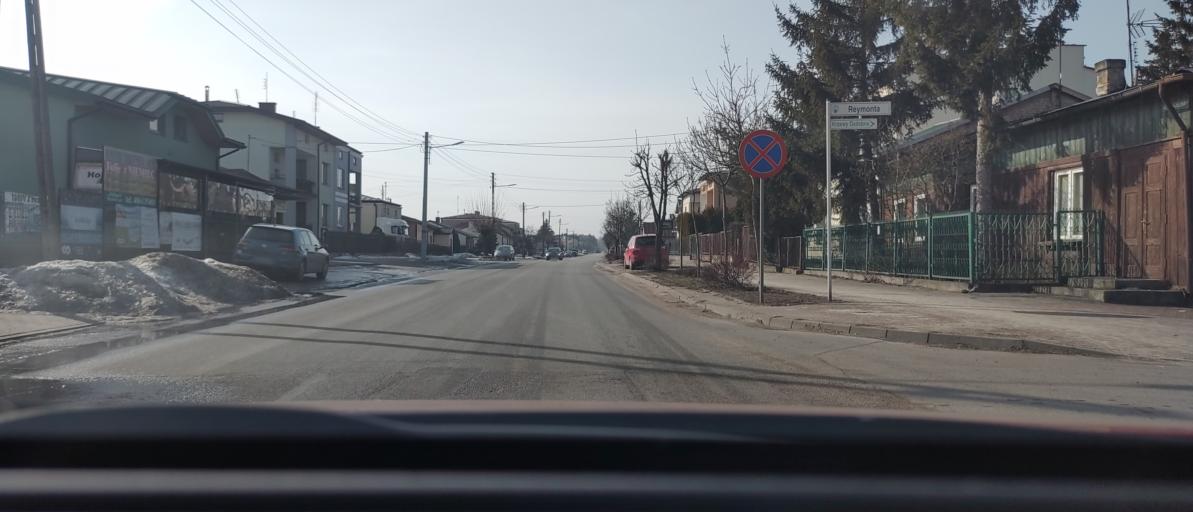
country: PL
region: Masovian Voivodeship
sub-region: Powiat bialobrzeski
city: Bialobrzegi
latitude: 51.6489
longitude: 20.9478
